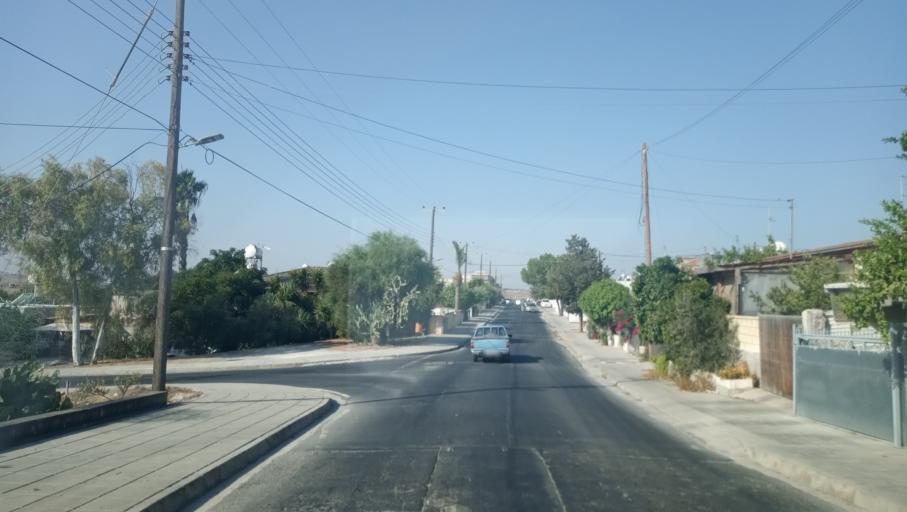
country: CY
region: Lefkosia
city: Geri
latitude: 35.1017
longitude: 33.4189
